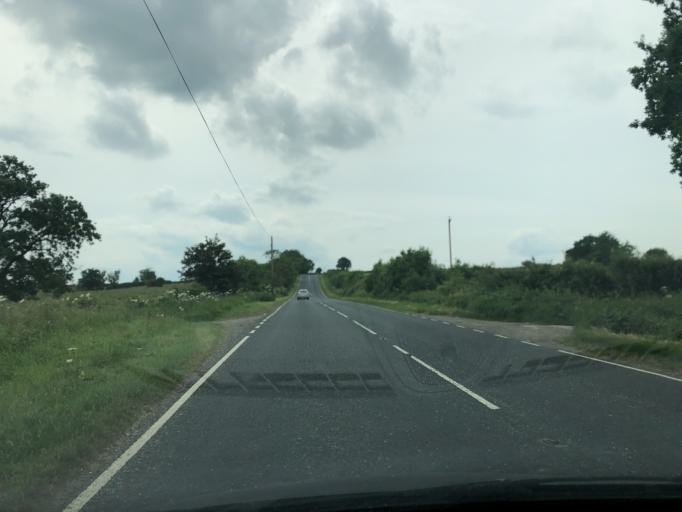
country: GB
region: England
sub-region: North Yorkshire
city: Pickering
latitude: 54.2607
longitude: -0.8365
